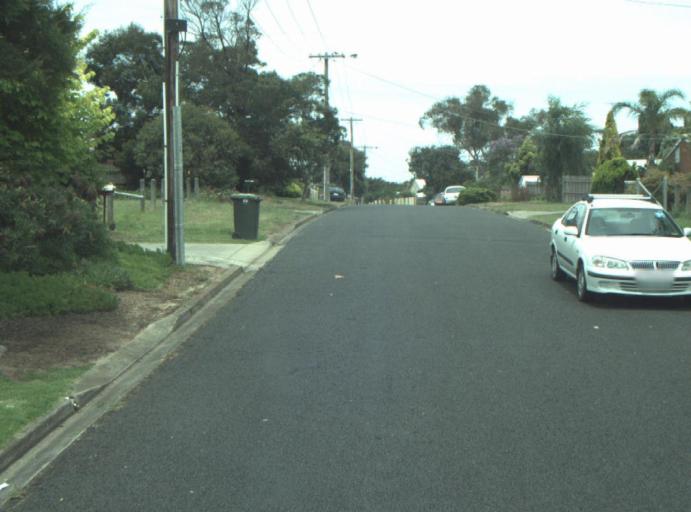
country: AU
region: Victoria
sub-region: Greater Geelong
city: Clifton Springs
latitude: -38.1616
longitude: 144.5520
